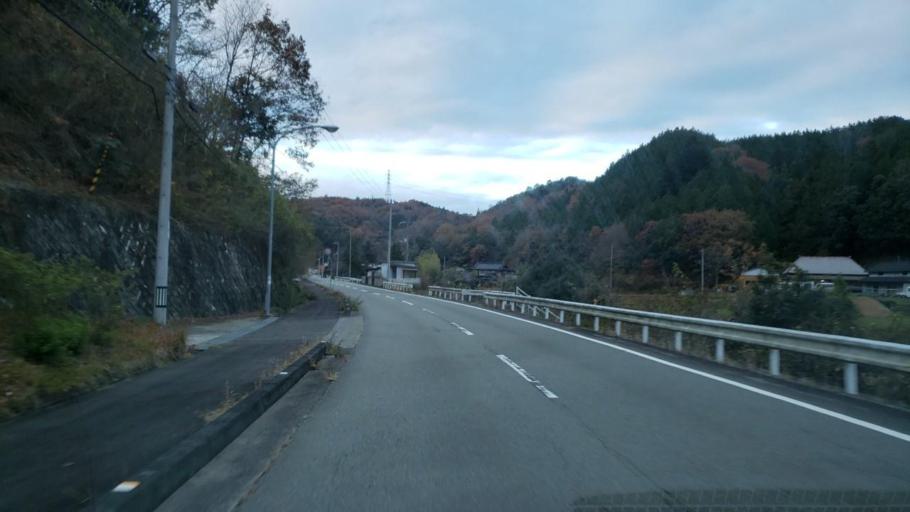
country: JP
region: Tokushima
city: Kamojimacho-jogejima
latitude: 34.1883
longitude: 134.2512
